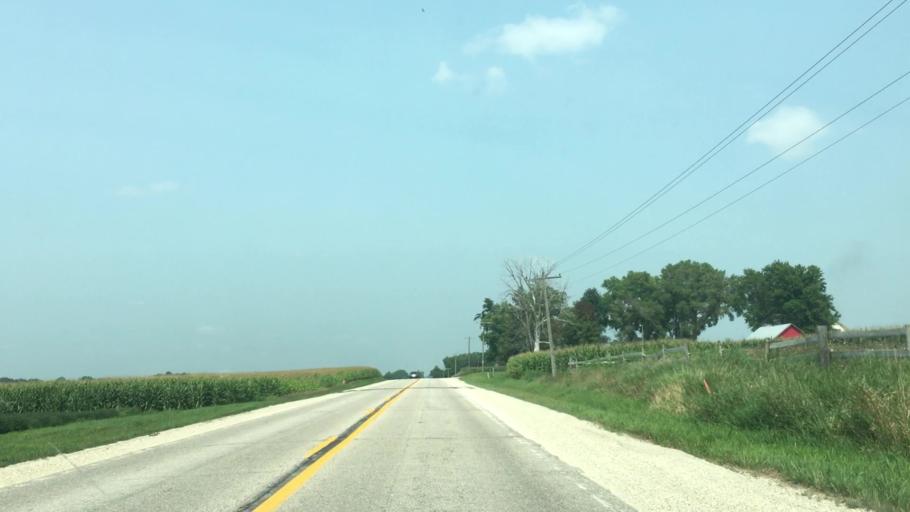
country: US
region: Iowa
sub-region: Benton County
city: Urbana
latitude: 42.3448
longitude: -91.8893
